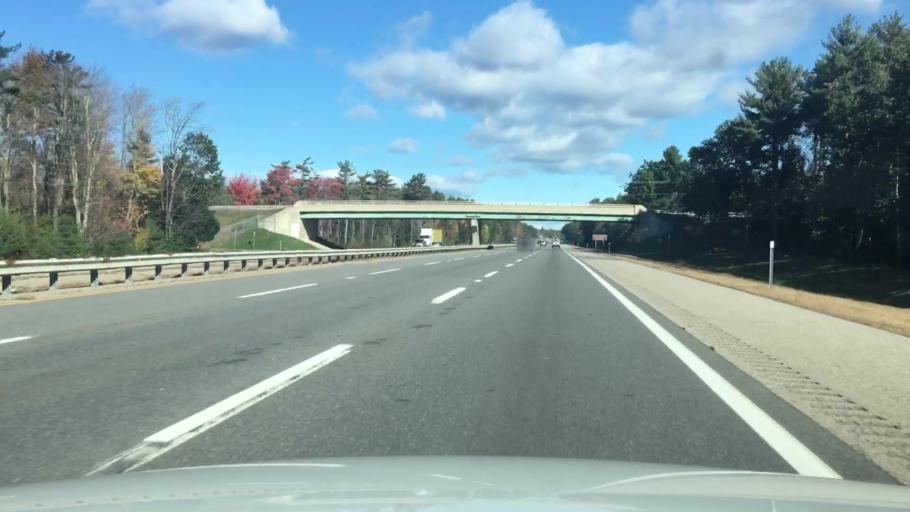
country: US
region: Maine
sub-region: York County
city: Wells Beach Station
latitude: 43.2965
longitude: -70.6159
